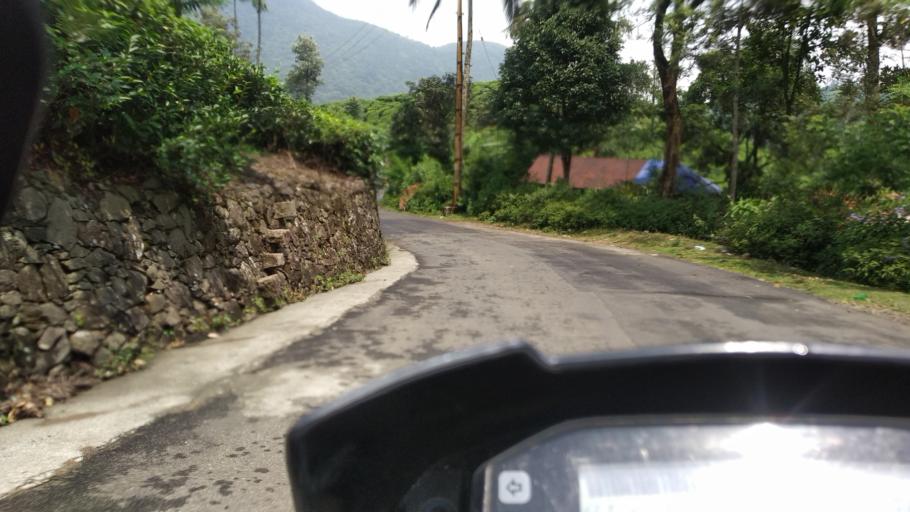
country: IN
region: Kerala
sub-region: Kottayam
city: Erattupetta
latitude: 9.6270
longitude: 76.9661
